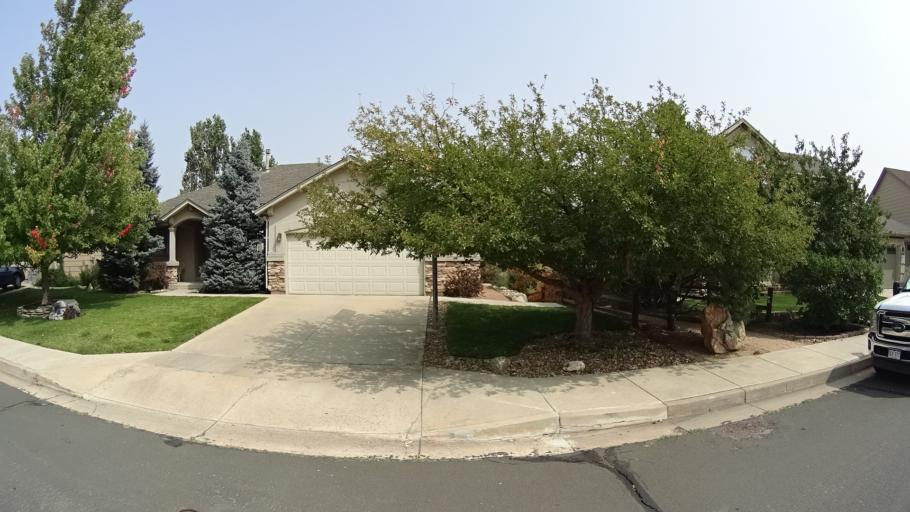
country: US
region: Colorado
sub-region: El Paso County
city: Cimarron Hills
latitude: 38.9186
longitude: -104.7463
